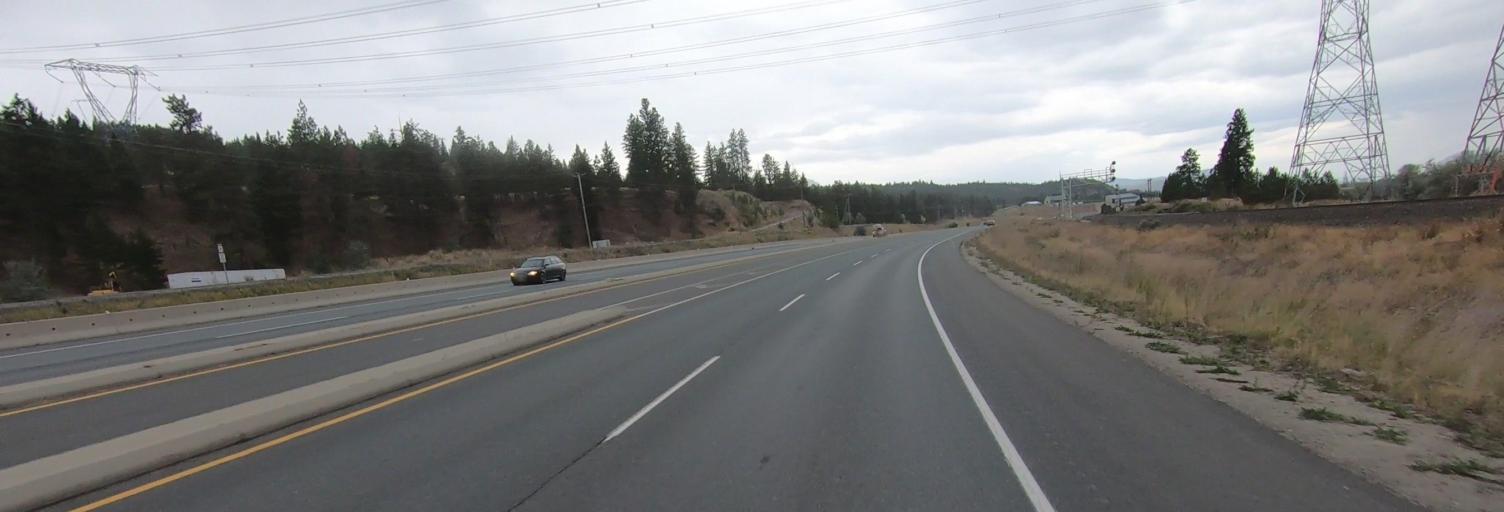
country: CA
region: British Columbia
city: Chase
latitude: 50.6457
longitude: -119.9065
